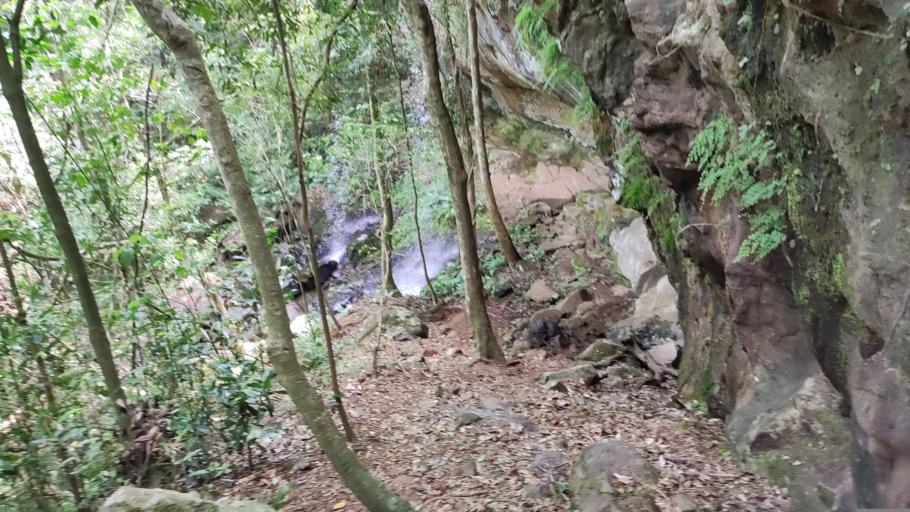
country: AR
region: Misiones
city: Dos de Mayo
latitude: -26.9967
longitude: -54.6240
